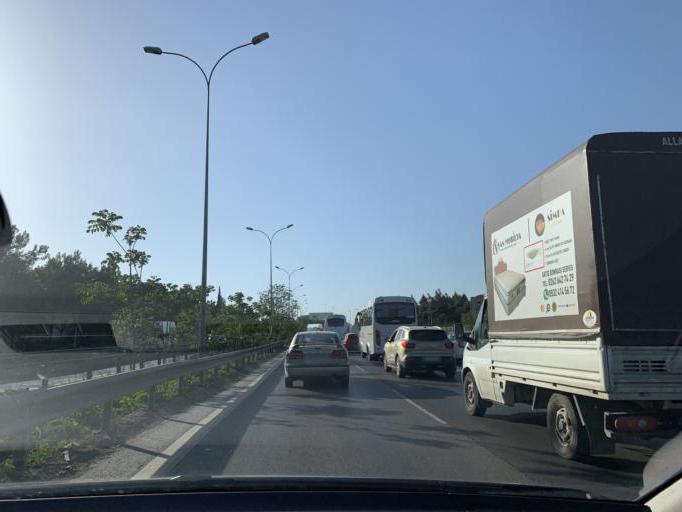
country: TR
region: Kocaeli
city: Darica
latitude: 40.8186
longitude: 29.3597
